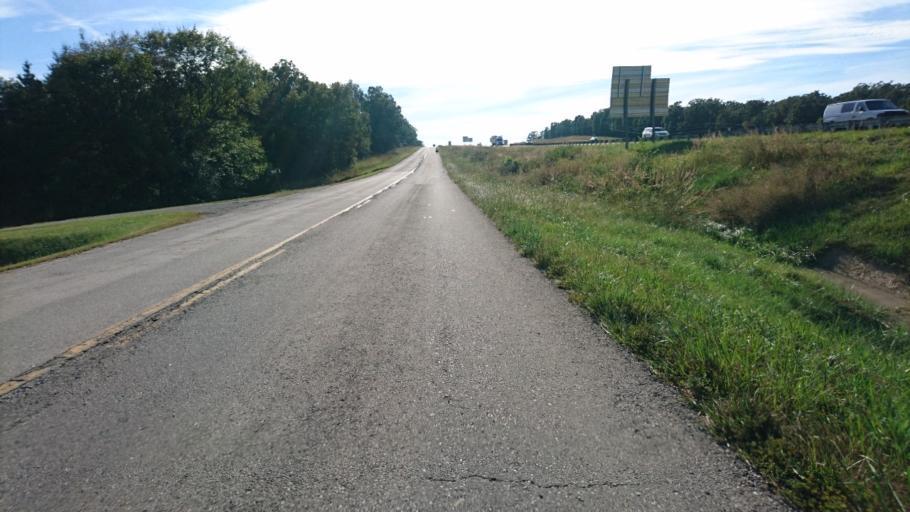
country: US
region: Missouri
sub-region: Crawford County
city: Bourbon
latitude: 38.1172
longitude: -91.3200
